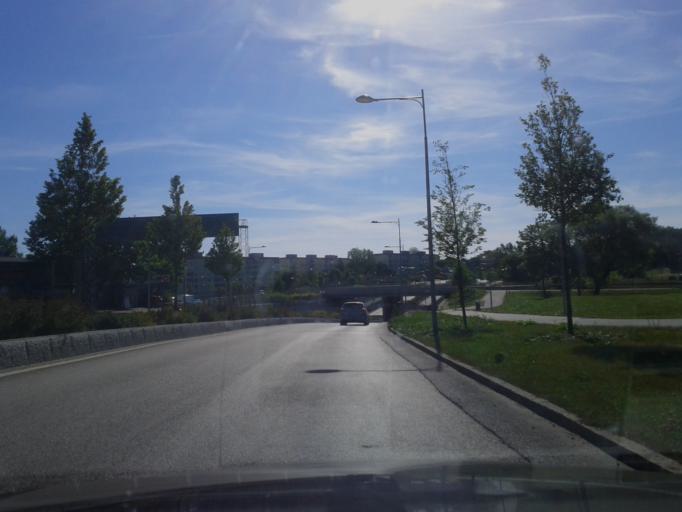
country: SE
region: Stockholm
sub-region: Taby Kommun
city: Taby
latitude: 59.4486
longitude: 18.0915
